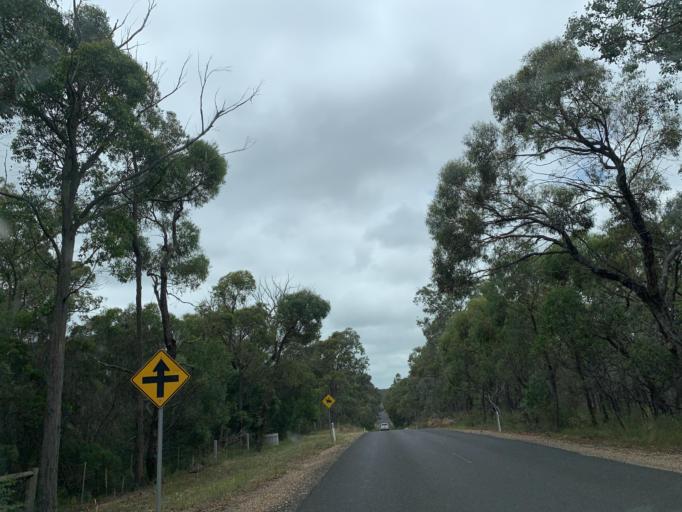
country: AU
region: Victoria
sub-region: Wellington
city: Heyfield
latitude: -37.9342
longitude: 146.7876
